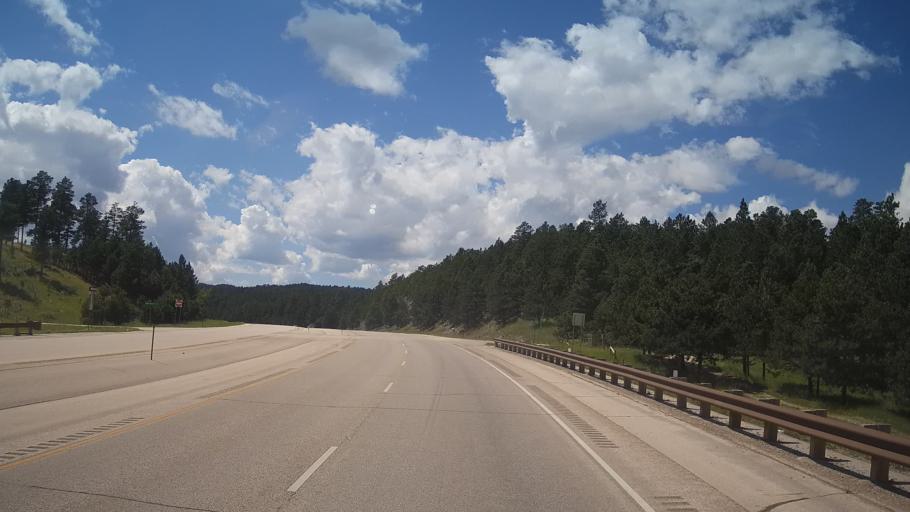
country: US
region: South Dakota
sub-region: Pennington County
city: Colonial Pine Hills
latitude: 43.9399
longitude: -103.4100
